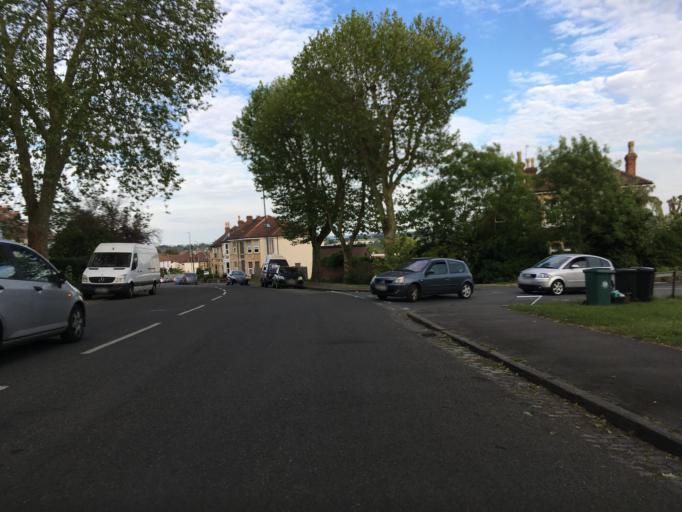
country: GB
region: England
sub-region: Bristol
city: Bristol
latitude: 51.4875
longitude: -2.5890
